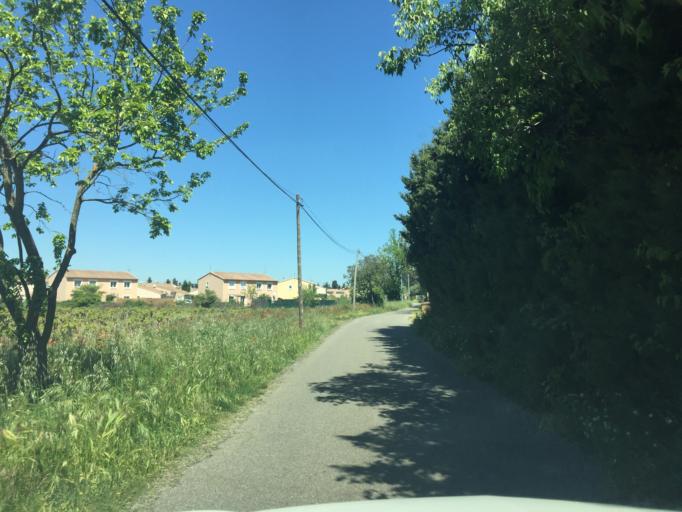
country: FR
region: Provence-Alpes-Cote d'Azur
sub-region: Departement du Vaucluse
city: Orange
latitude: 44.1163
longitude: 4.7999
